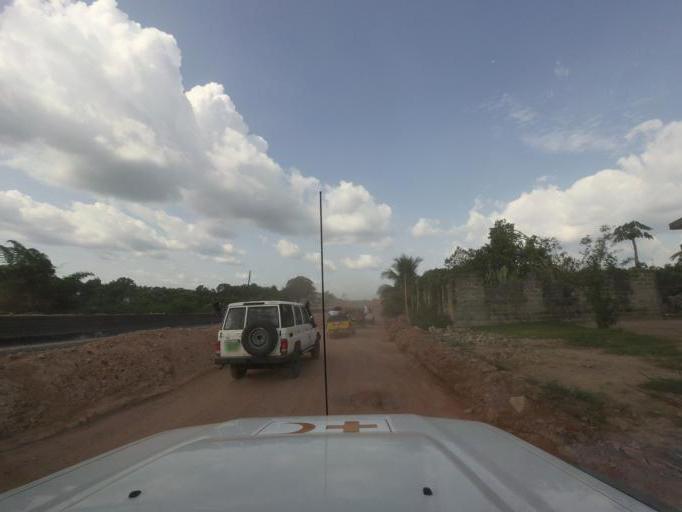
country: LR
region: Bong
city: Gbarnga
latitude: 7.0351
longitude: -9.5519
